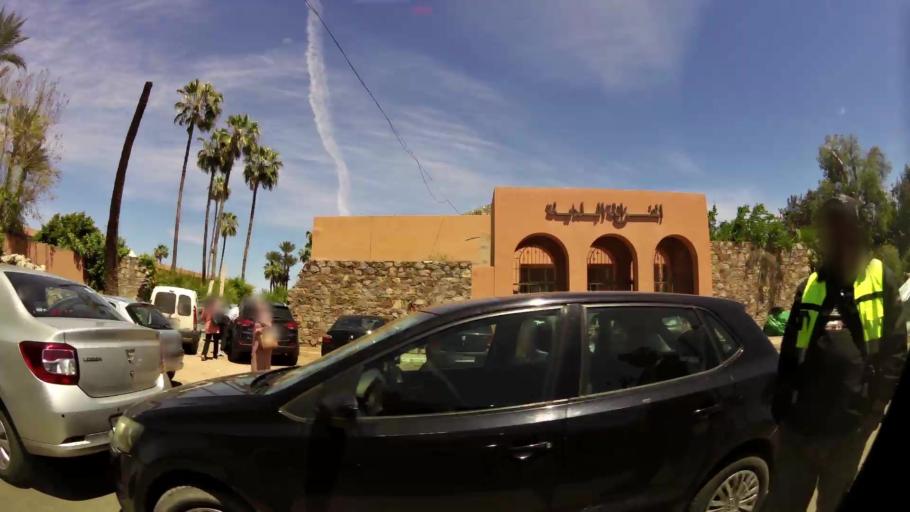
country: MA
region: Marrakech-Tensift-Al Haouz
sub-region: Marrakech
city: Marrakesh
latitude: 31.6229
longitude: -7.9969
